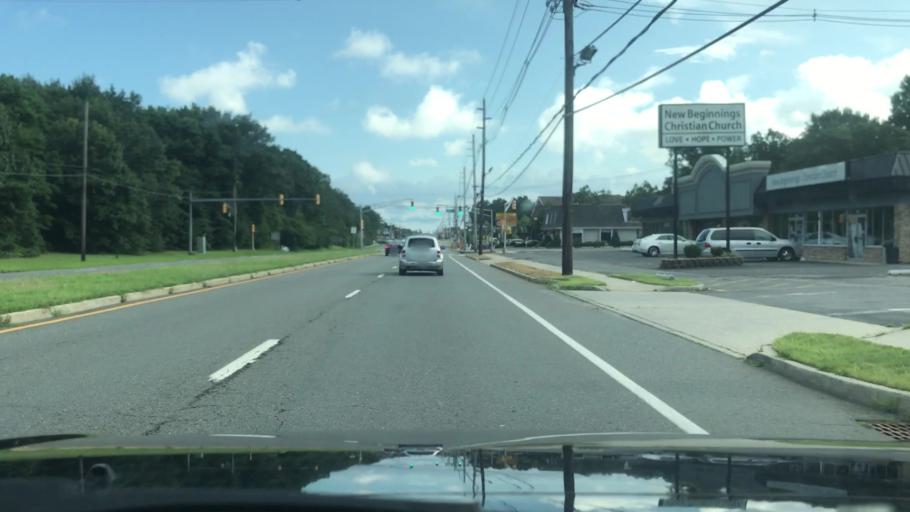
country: US
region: New Jersey
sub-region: Ocean County
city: Leisure Village East
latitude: 40.0361
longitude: -74.1430
